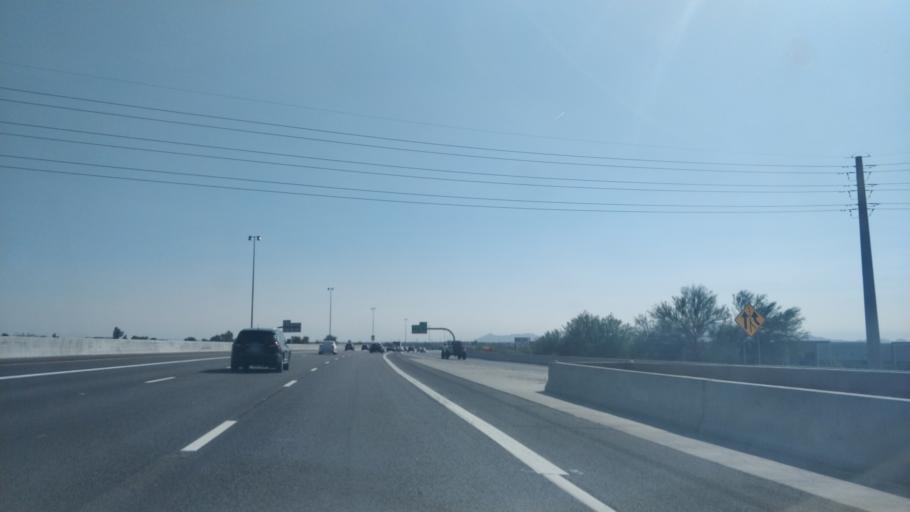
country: US
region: Arizona
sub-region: Maricopa County
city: Chandler
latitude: 33.2863
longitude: -111.8373
